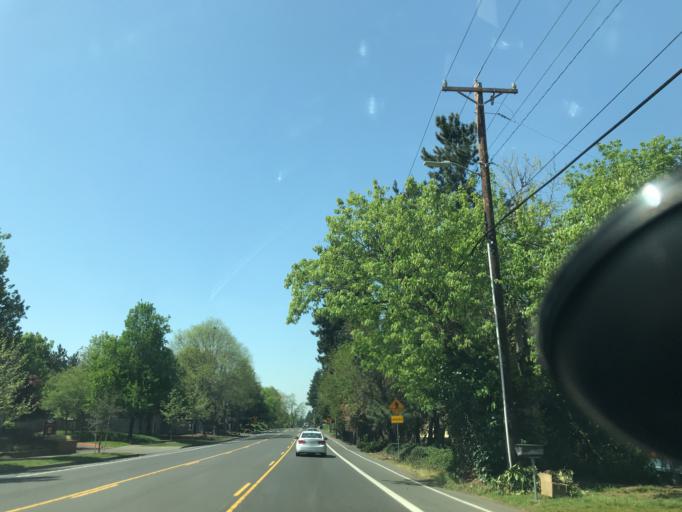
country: US
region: Oregon
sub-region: Multnomah County
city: Gresham
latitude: 45.4931
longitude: -122.4882
